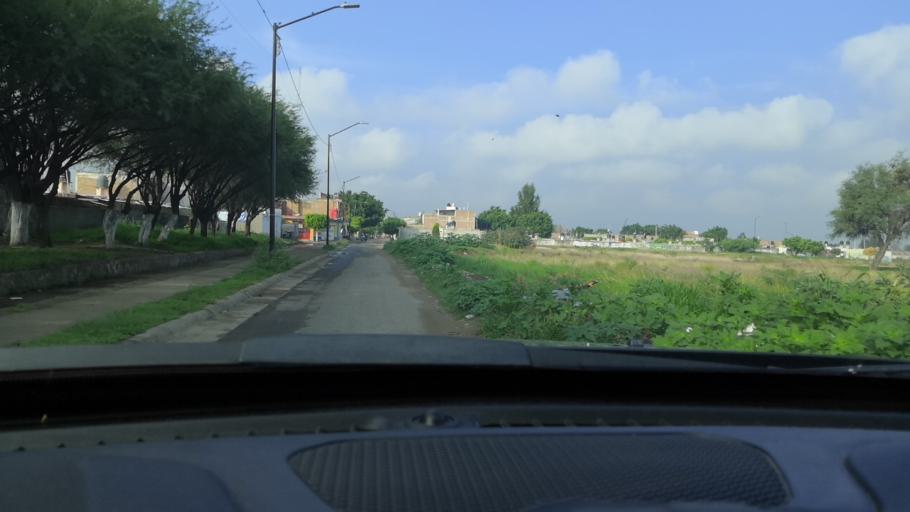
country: MX
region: Guanajuato
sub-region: Leon
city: Fraccionamiento Paraiso Real
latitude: 21.1025
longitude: -101.5877
